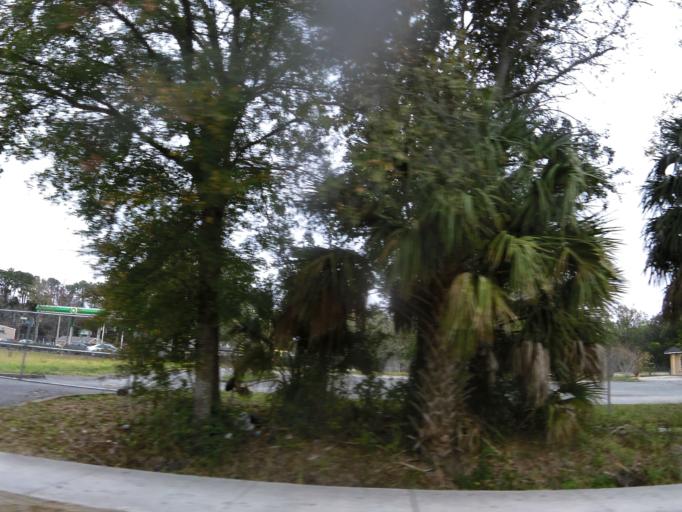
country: US
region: Florida
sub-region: Duval County
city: Jacksonville
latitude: 30.3738
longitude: -81.7148
